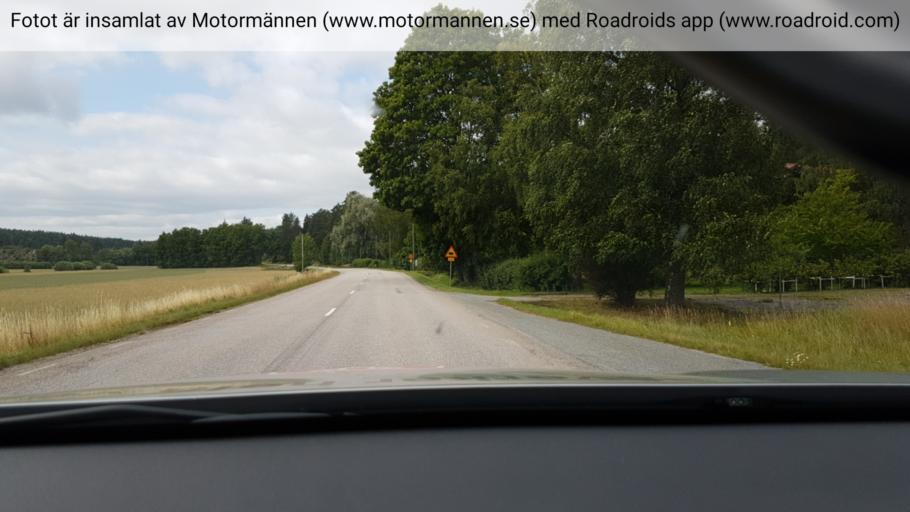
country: SE
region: Stockholm
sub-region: Norrtalje Kommun
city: Rimbo
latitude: 59.7261
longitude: 18.4831
